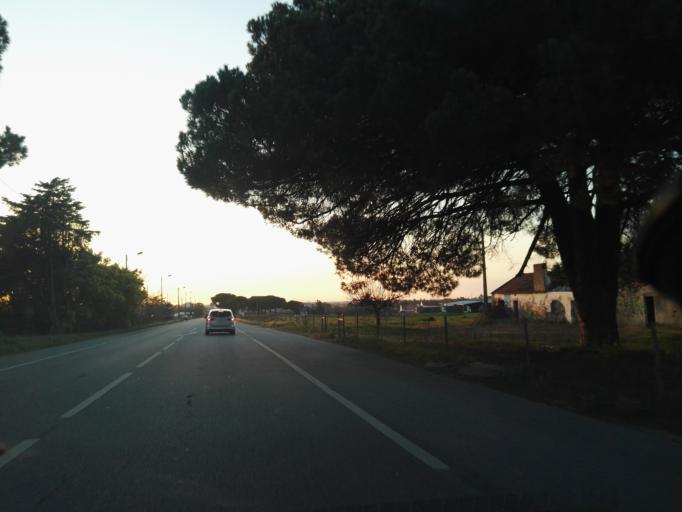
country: PT
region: Evora
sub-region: Vendas Novas
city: Vendas Novas
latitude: 38.6829
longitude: -8.5987
